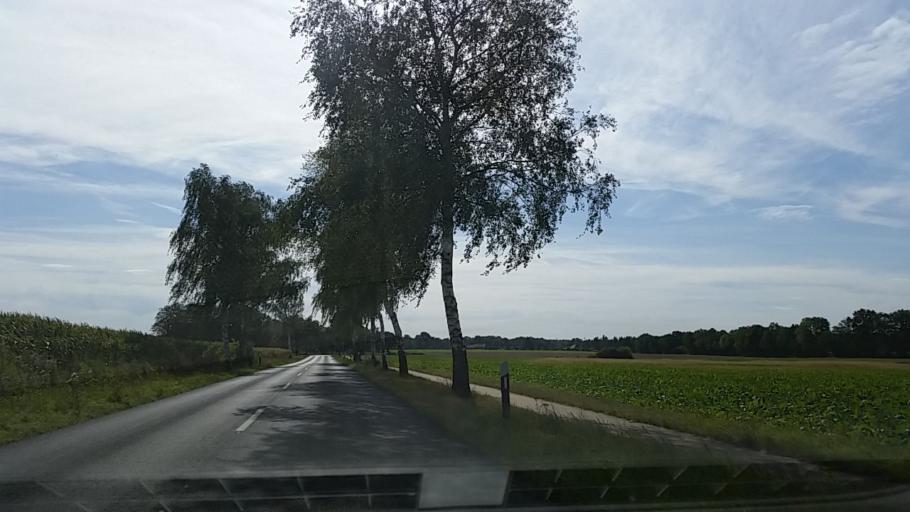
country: DE
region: Lower Saxony
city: Embsen
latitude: 53.1888
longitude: 10.3471
